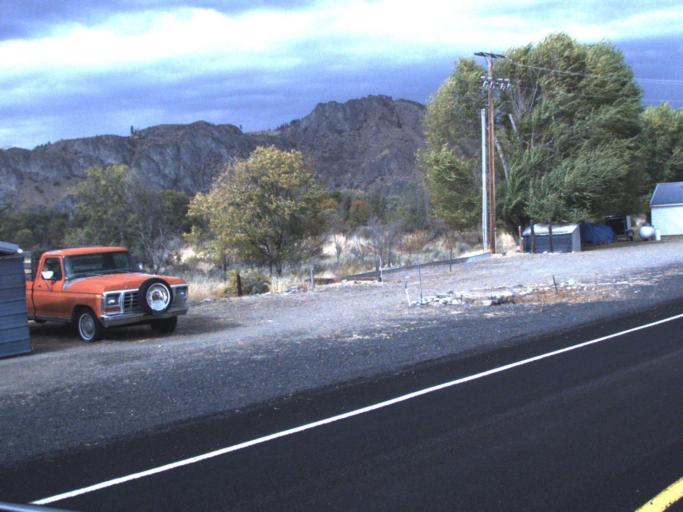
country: US
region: Washington
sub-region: Okanogan County
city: Coulee Dam
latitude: 47.9259
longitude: -118.6896
